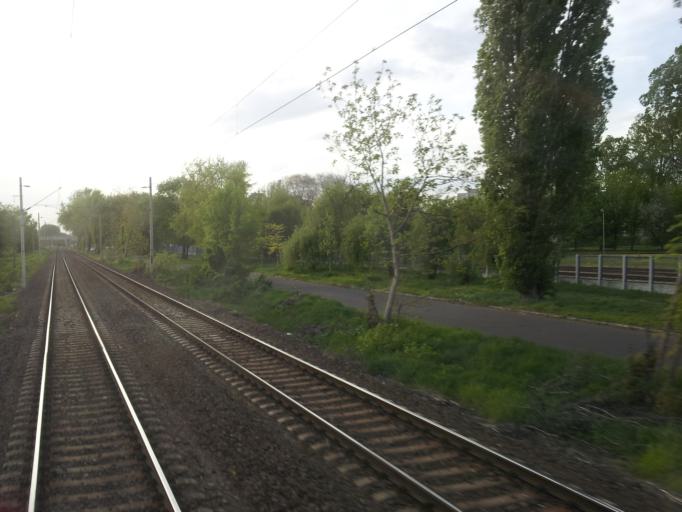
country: HU
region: Budapest
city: Budapest XIV. keruelet
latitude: 47.5290
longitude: 19.1353
